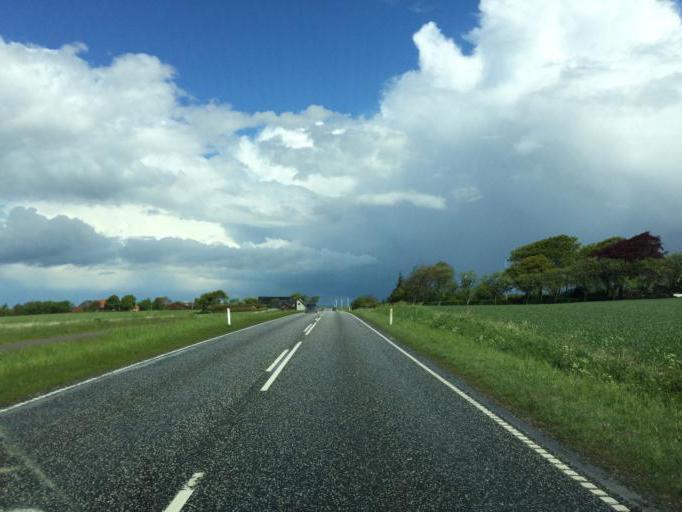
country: DK
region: Central Jutland
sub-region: Holstebro Kommune
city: Vinderup
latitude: 56.4562
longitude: 8.7660
